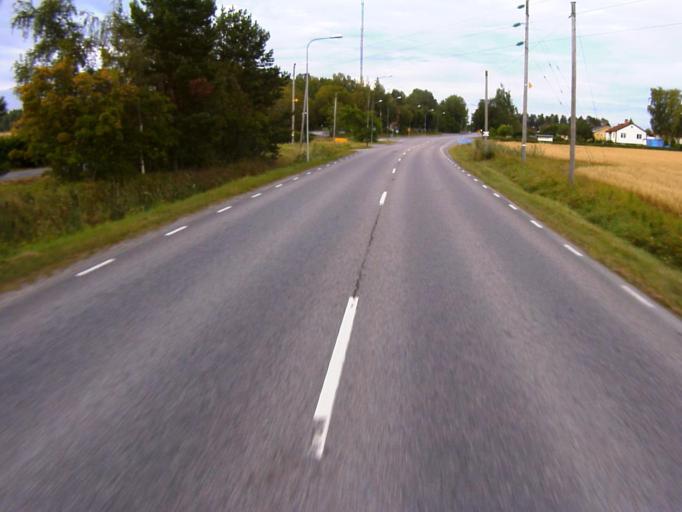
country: SE
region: Soedermanland
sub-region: Eskilstuna Kommun
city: Torshalla
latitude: 59.4028
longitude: 16.4851
